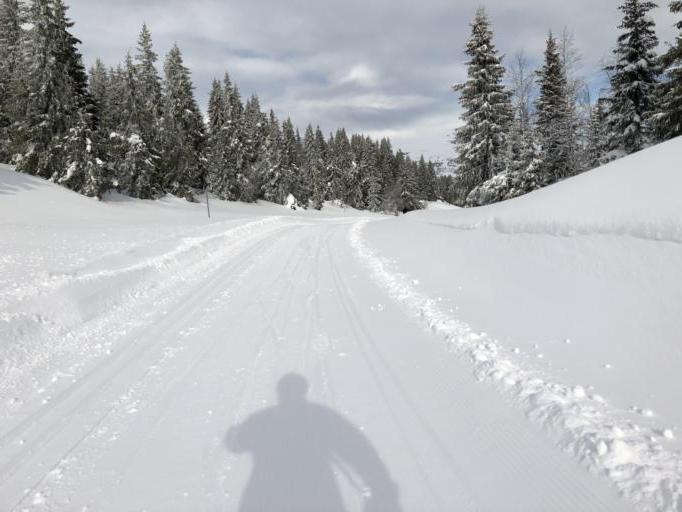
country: NO
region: Oppland
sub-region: Gausdal
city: Segalstad bru
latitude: 61.3125
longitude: 10.0719
